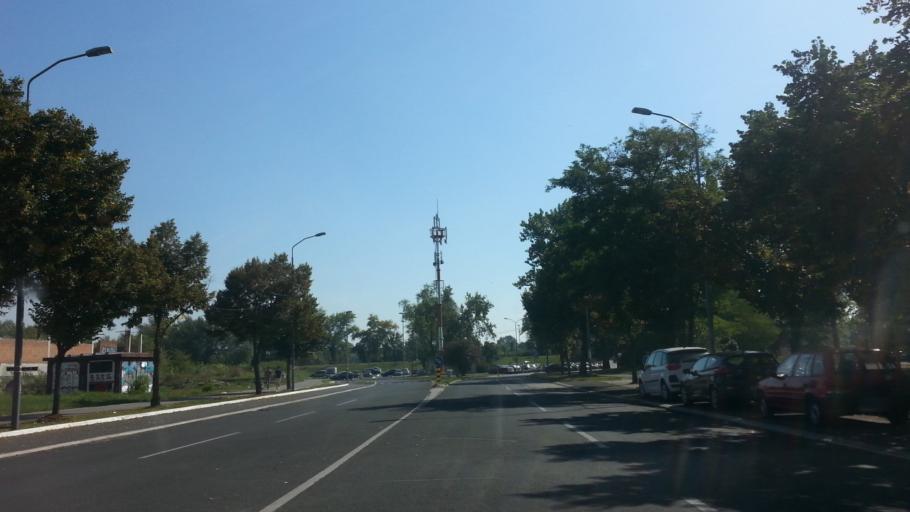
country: RS
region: Central Serbia
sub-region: Belgrade
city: Cukarica
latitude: 44.7969
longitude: 20.3840
